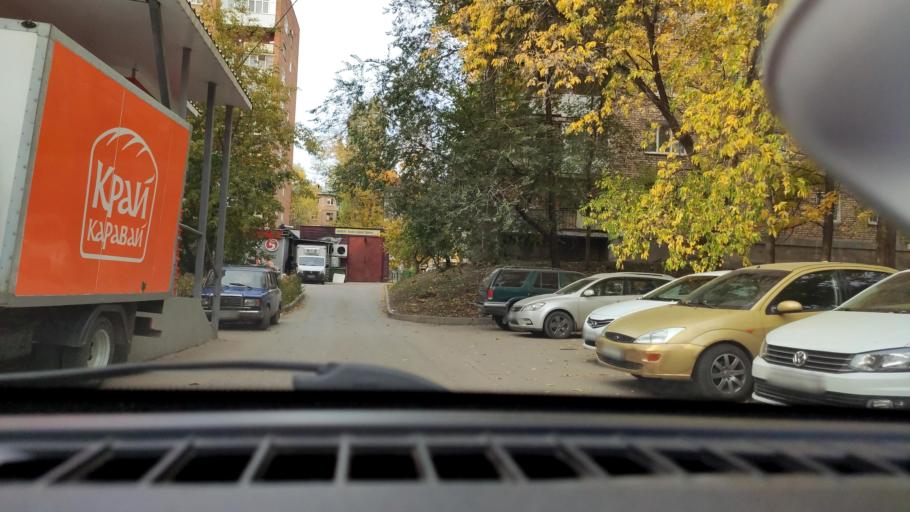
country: RU
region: Samara
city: Samara
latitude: 53.2432
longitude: 50.2196
